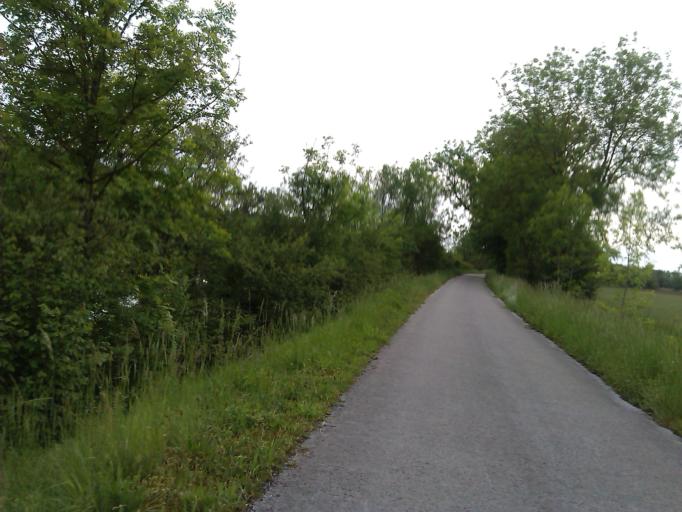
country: FR
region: Franche-Comte
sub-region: Departement du Jura
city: Fraisans
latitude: 47.1638
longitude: 5.7783
